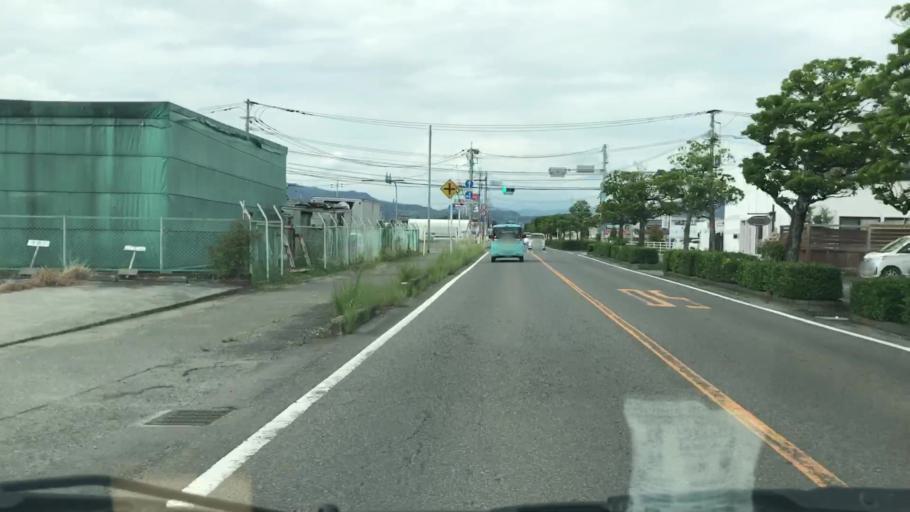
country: JP
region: Saga Prefecture
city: Saga-shi
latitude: 33.2718
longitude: 130.2611
